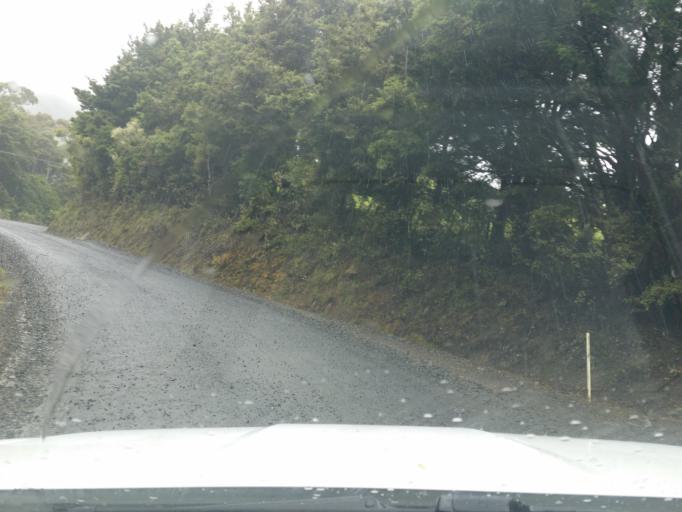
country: NZ
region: Northland
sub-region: Kaipara District
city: Dargaville
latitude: -35.7799
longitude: 173.9889
